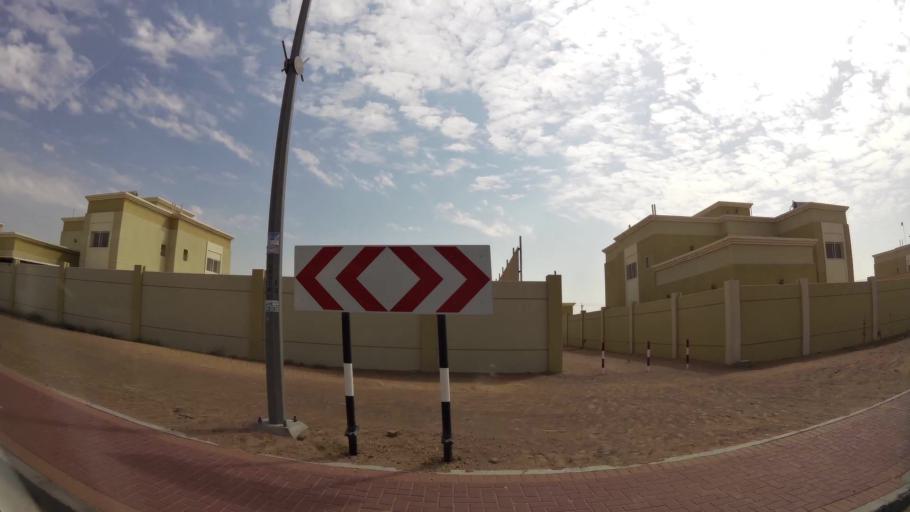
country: AE
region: Abu Dhabi
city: Al Ain
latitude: 24.0948
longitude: 55.8954
